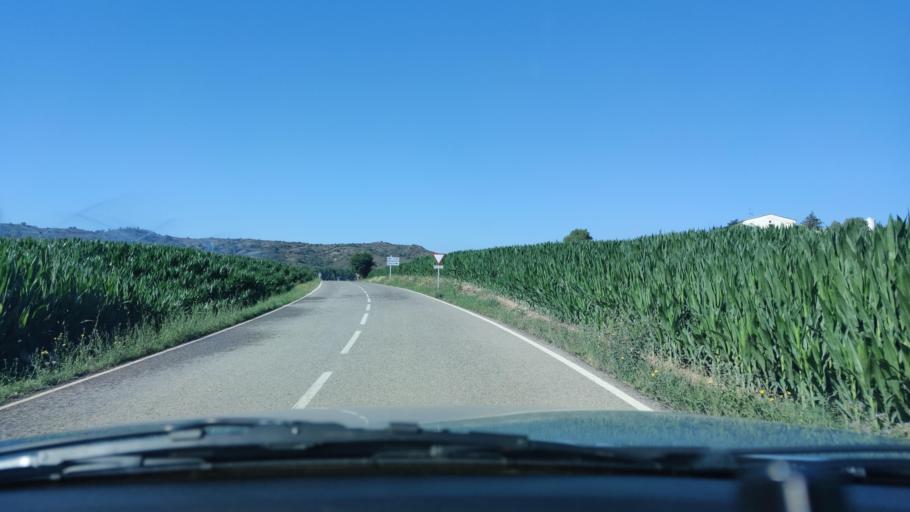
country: ES
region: Catalonia
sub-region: Provincia de Lleida
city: Ponts
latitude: 41.8918
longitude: 1.2326
